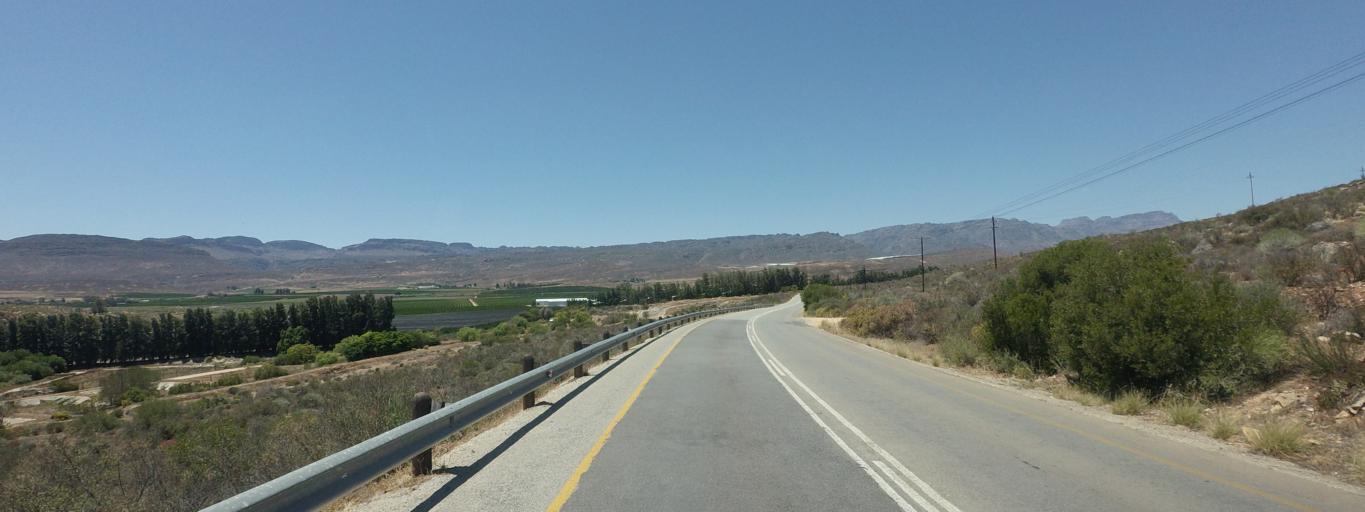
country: ZA
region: Western Cape
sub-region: West Coast District Municipality
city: Clanwilliam
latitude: -32.1703
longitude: 18.8747
